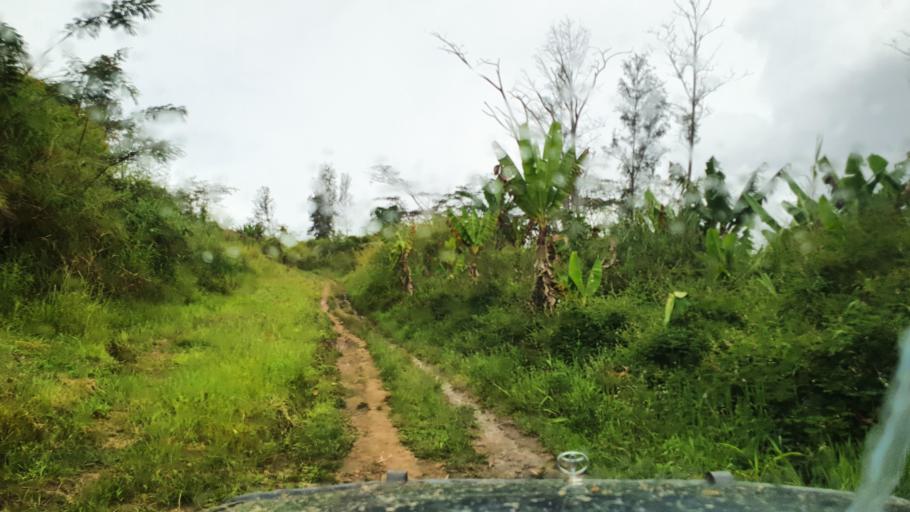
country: PG
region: Jiwaka
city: Minj
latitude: -5.9542
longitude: 144.7784
